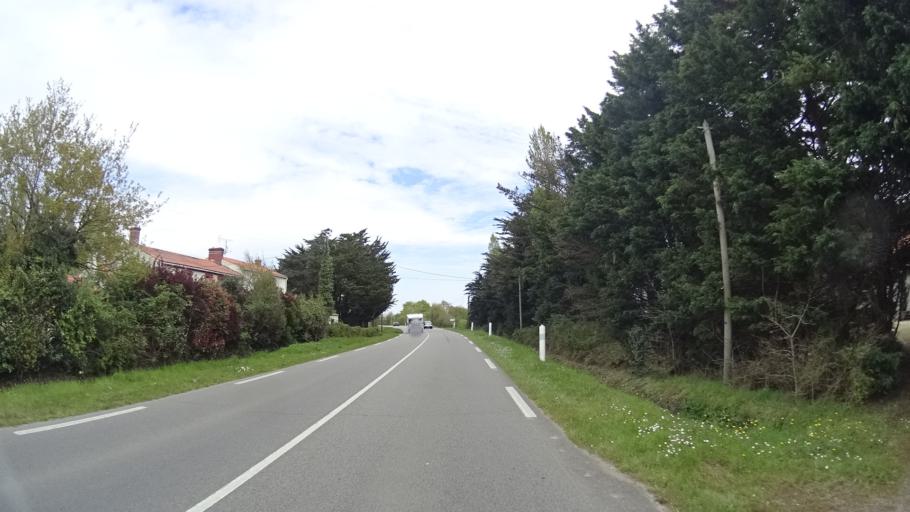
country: FR
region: Pays de la Loire
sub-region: Departement de la Loire-Atlantique
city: Bourgneuf-en-Retz
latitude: 47.0655
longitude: -1.9109
